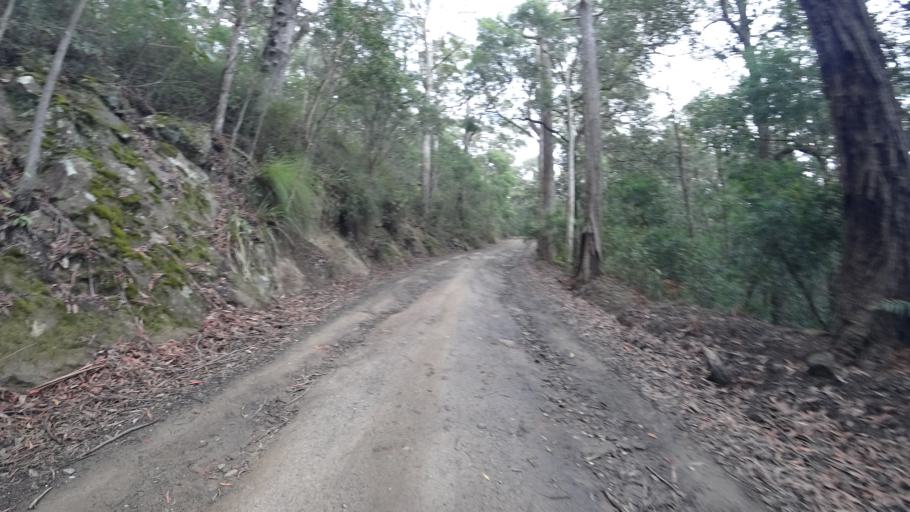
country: AU
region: New South Wales
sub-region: Shoalhaven Shire
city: Milton
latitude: -35.1733
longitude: 150.3734
